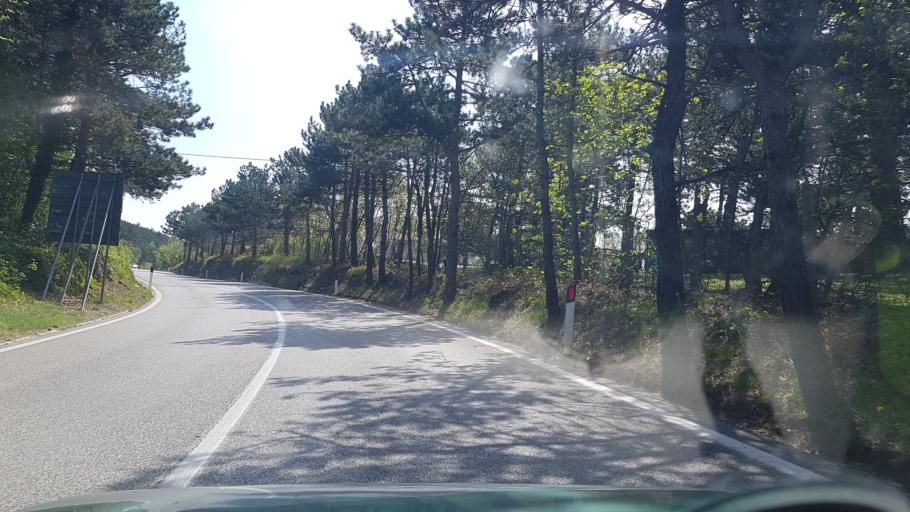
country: IT
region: Friuli Venezia Giulia
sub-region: Provincia di Trieste
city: Dolina
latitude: 45.6321
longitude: 13.8866
